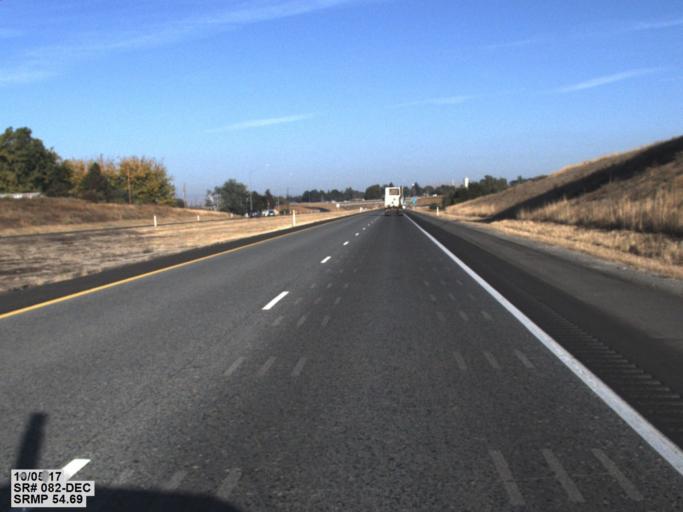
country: US
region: Washington
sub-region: Yakima County
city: Zillah
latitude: 46.3860
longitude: -120.2314
